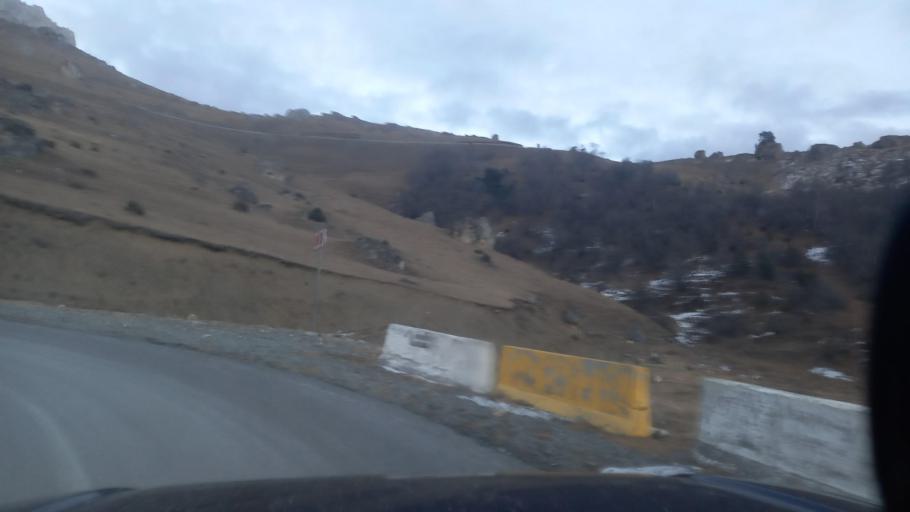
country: RU
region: Ingushetiya
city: Dzhayrakh
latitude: 42.8206
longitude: 44.8268
